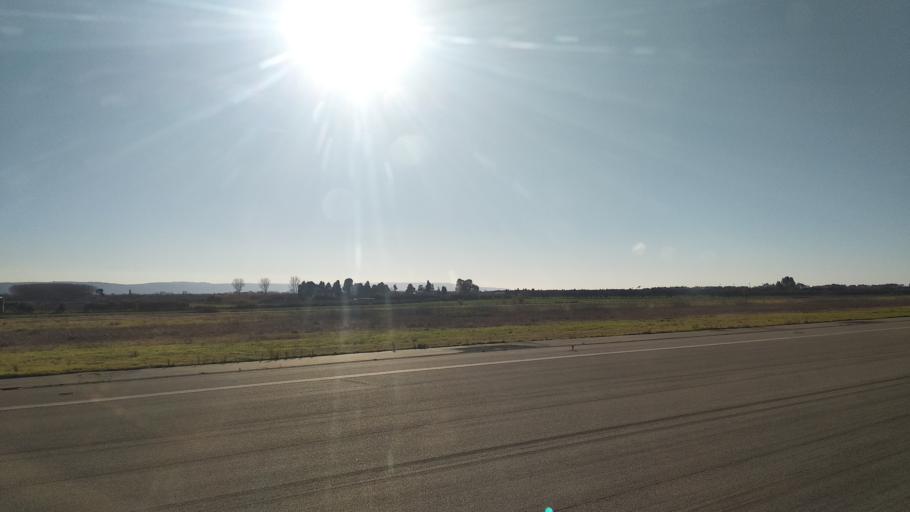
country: IT
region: Calabria
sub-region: Provincia di Catanzaro
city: Santa Eufemia Lamezia
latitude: 38.9047
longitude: 16.2491
